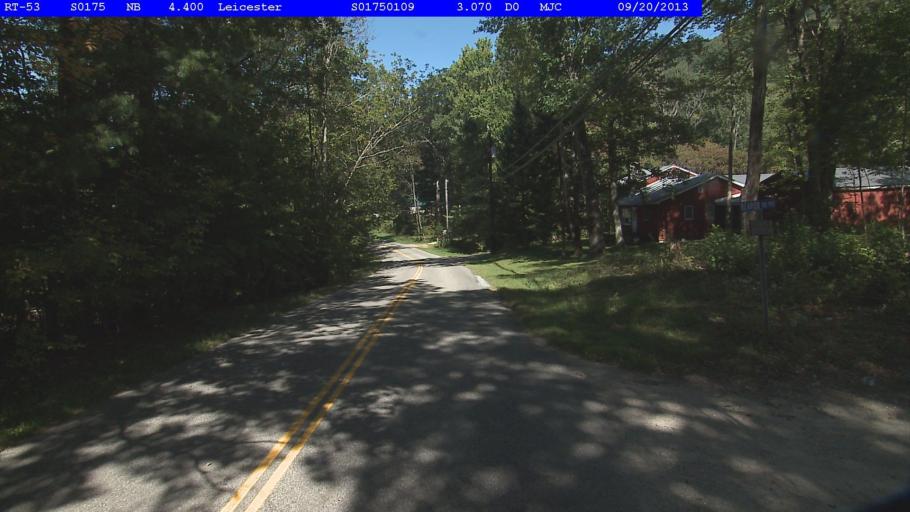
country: US
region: Vermont
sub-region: Rutland County
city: Brandon
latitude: 43.8868
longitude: -73.0643
